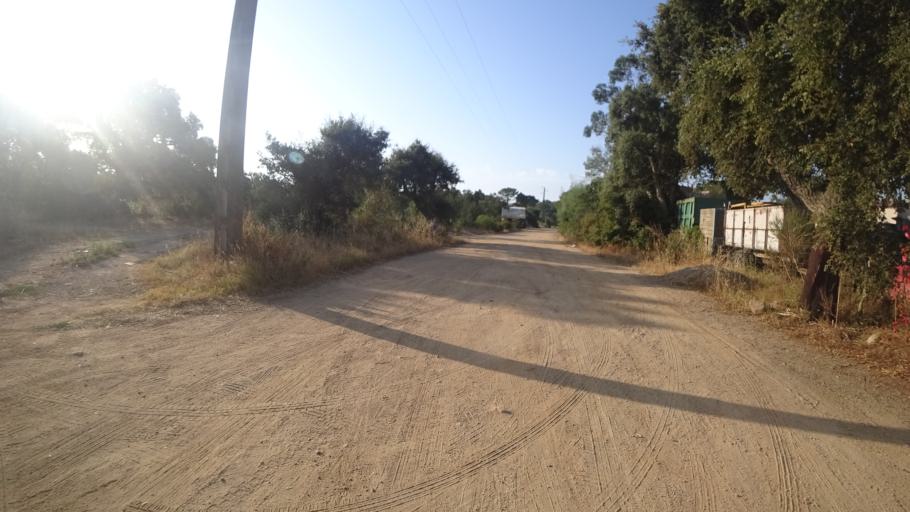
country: FR
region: Corsica
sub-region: Departement de la Corse-du-Sud
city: Porto-Vecchio
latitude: 41.6410
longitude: 9.3463
